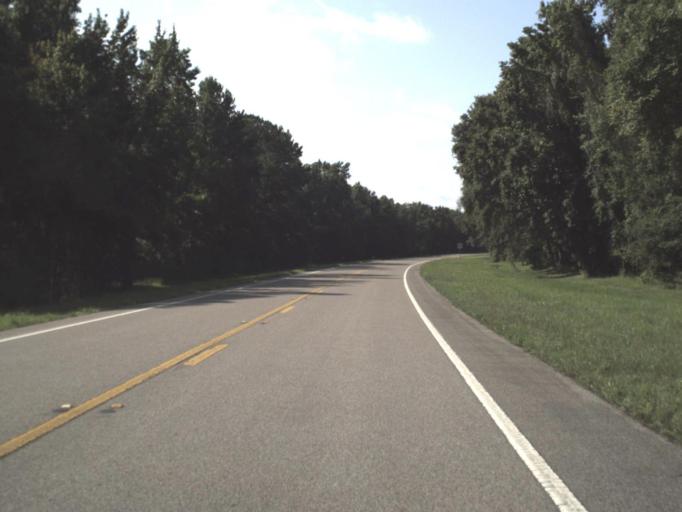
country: US
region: Florida
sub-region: Hernando County
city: North Brooksville
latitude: 28.6100
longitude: -82.4027
